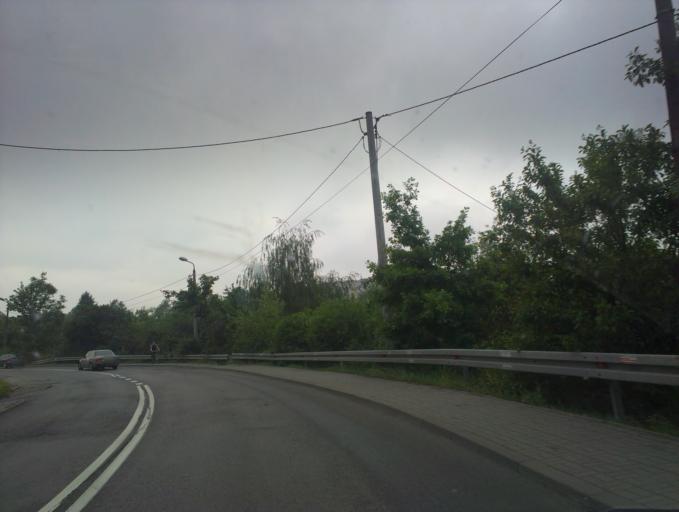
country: PL
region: Silesian Voivodeship
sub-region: Katowice
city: Katowice
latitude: 50.2438
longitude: 19.0207
